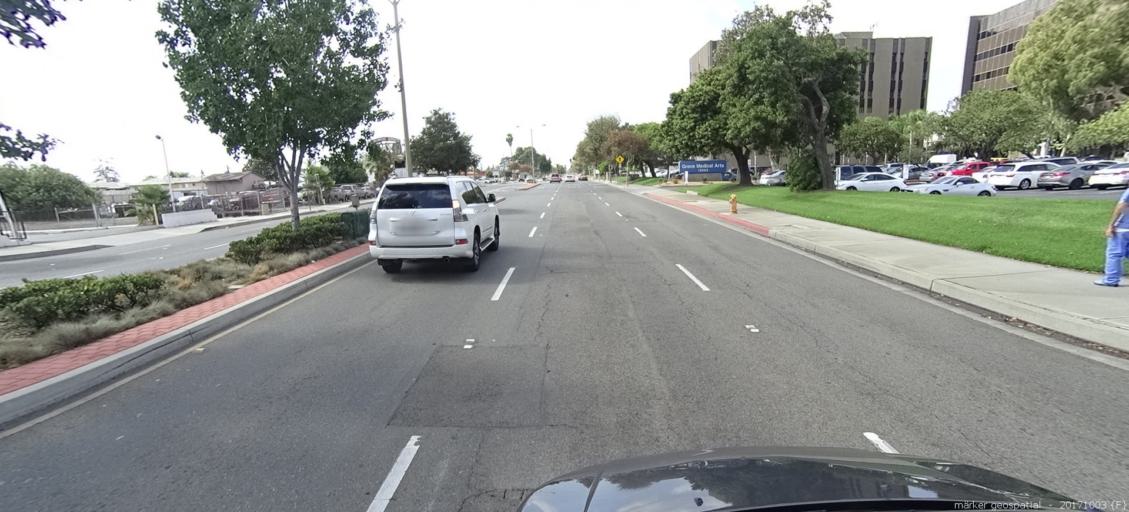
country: US
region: California
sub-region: Orange County
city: Garden Grove
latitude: 33.7745
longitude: -117.9113
